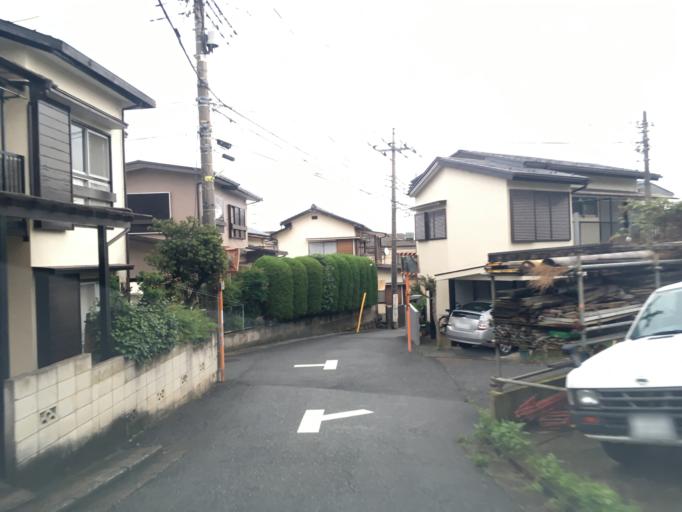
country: JP
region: Saitama
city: Tokorozawa
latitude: 35.7857
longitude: 139.4438
